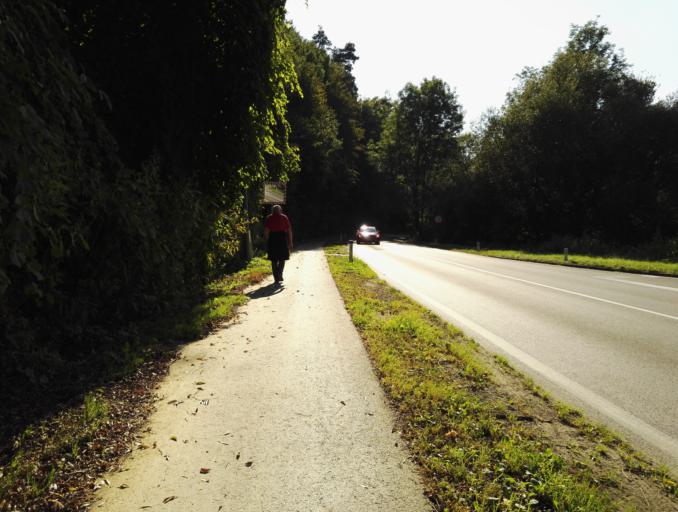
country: AT
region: Styria
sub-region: Politischer Bezirk Graz-Umgebung
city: Gratkorn
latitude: 47.1406
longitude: 15.3328
